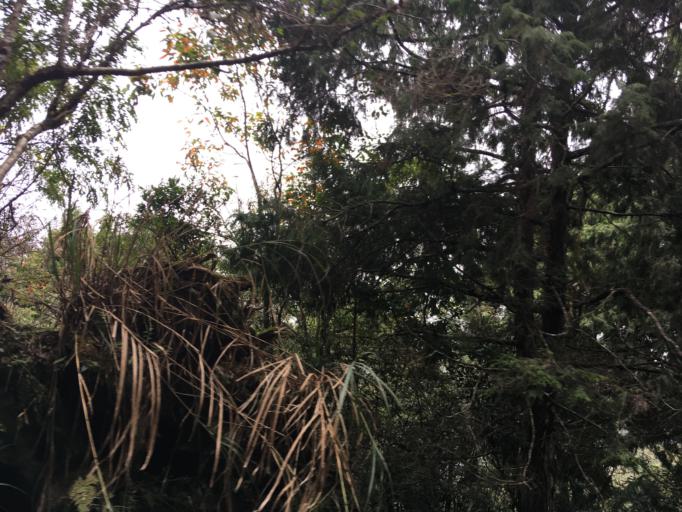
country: TW
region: Taiwan
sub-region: Yilan
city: Yilan
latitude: 24.4884
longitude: 121.5343
